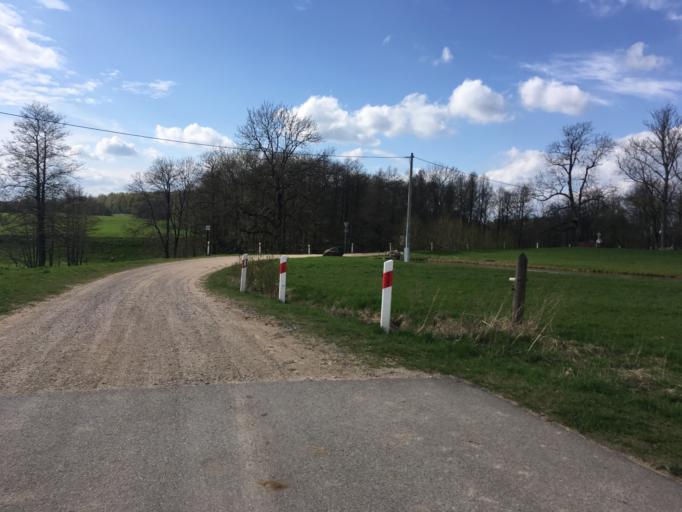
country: PL
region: Podlasie
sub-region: Powiat suwalski
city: Filipow
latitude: 54.3625
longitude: 22.7954
